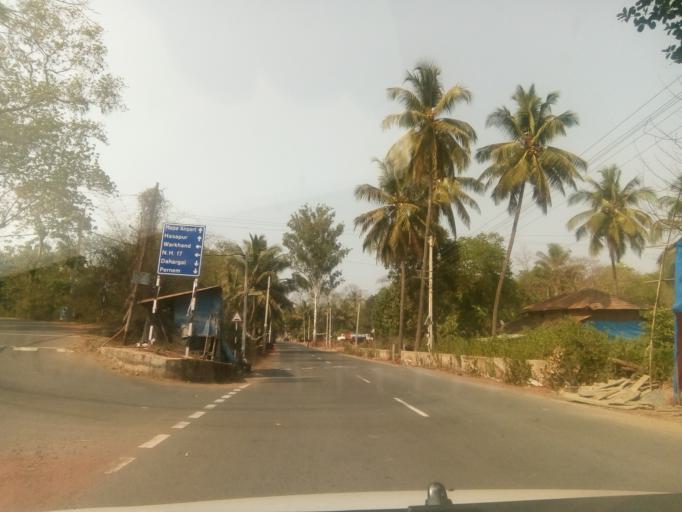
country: IN
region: Goa
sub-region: North Goa
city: Pernem
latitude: 15.7064
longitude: 73.8528
